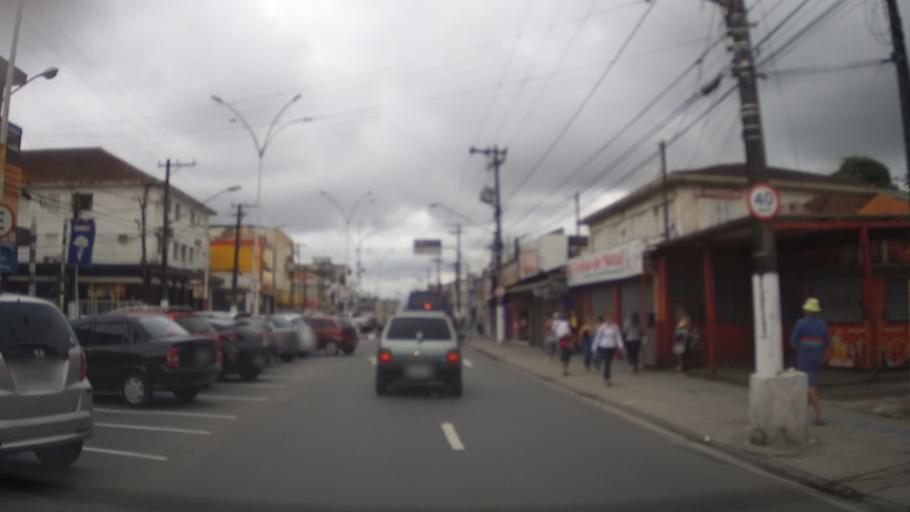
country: BR
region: Sao Paulo
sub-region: Santos
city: Santos
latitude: -23.9433
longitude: -46.3006
